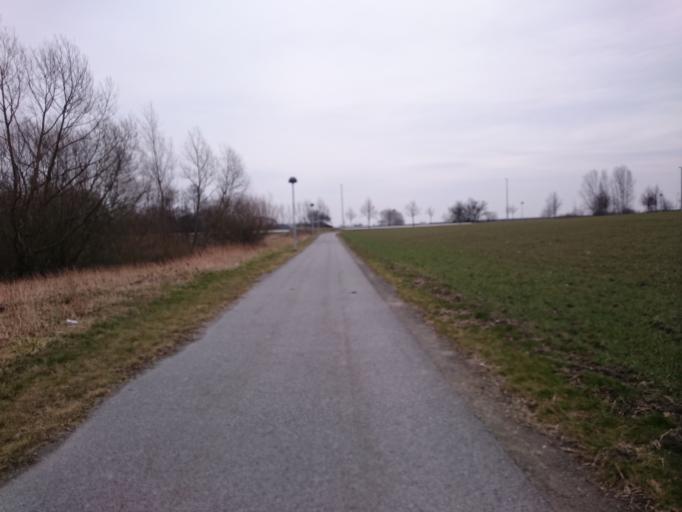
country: SE
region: Skane
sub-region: Lunds Kommun
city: Lund
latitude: 55.6819
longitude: 13.1831
